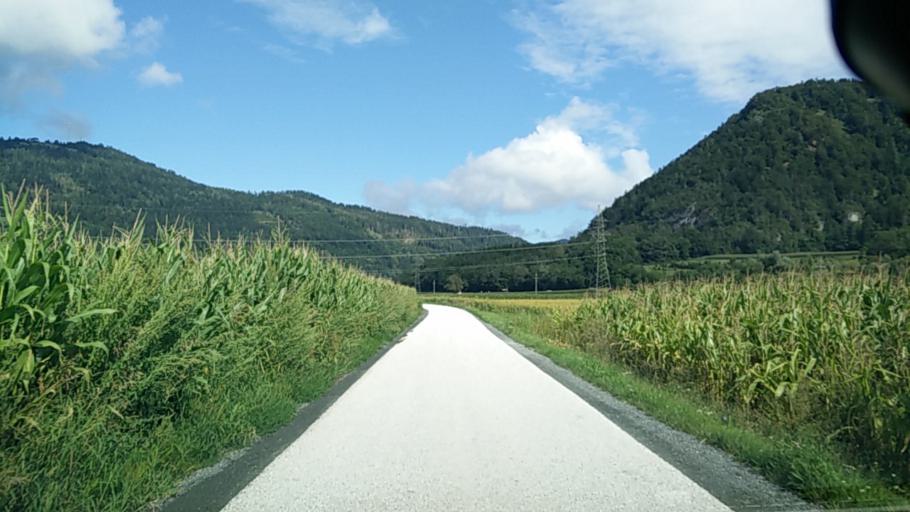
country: AT
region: Carinthia
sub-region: Politischer Bezirk Sankt Veit an der Glan
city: Bruckl
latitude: 46.7211
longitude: 14.5370
